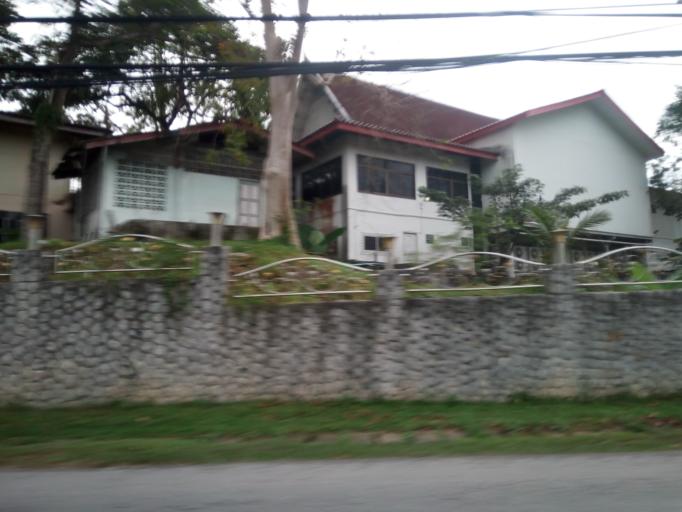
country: TH
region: Phuket
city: Thalang
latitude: 7.9886
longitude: 98.3559
